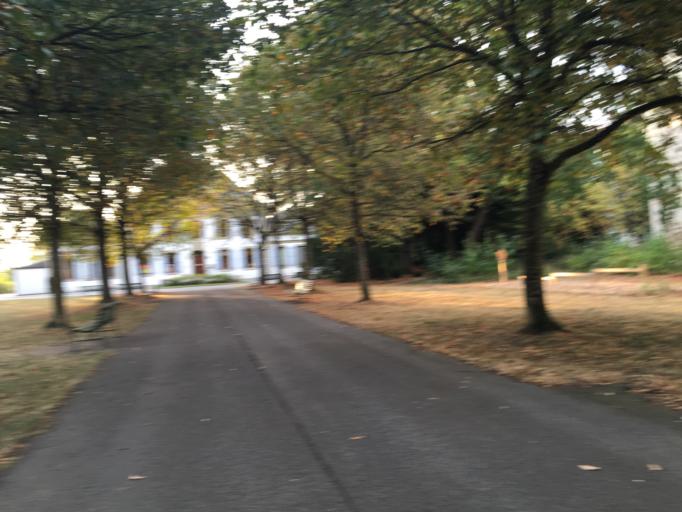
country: CH
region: Geneva
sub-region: Geneva
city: Geneve
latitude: 46.2148
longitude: 6.1363
